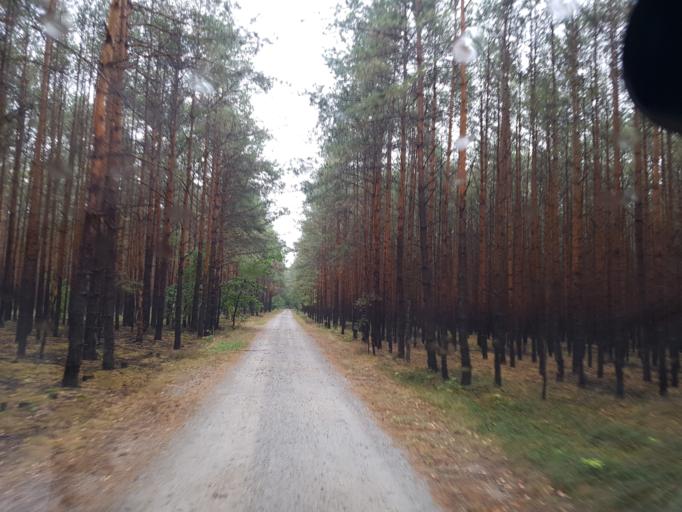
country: DE
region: Brandenburg
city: Finsterwalde
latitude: 51.6153
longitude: 13.7771
